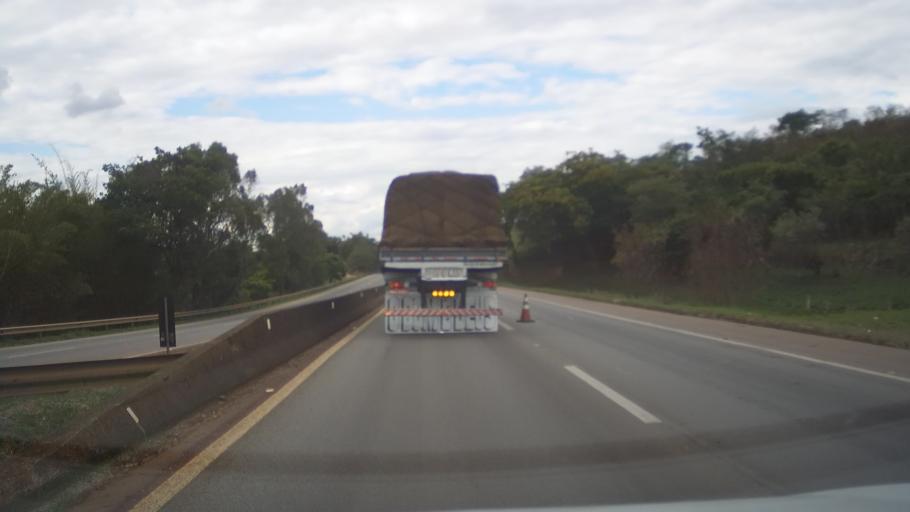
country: BR
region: Minas Gerais
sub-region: Itauna
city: Itauna
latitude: -20.3152
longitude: -44.4527
